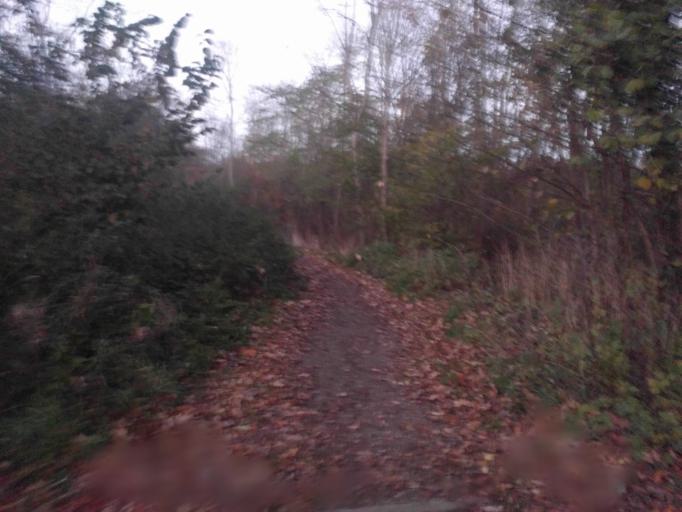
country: DK
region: South Denmark
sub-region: Fredericia Kommune
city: Snoghoj
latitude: 55.5387
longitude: 9.7218
